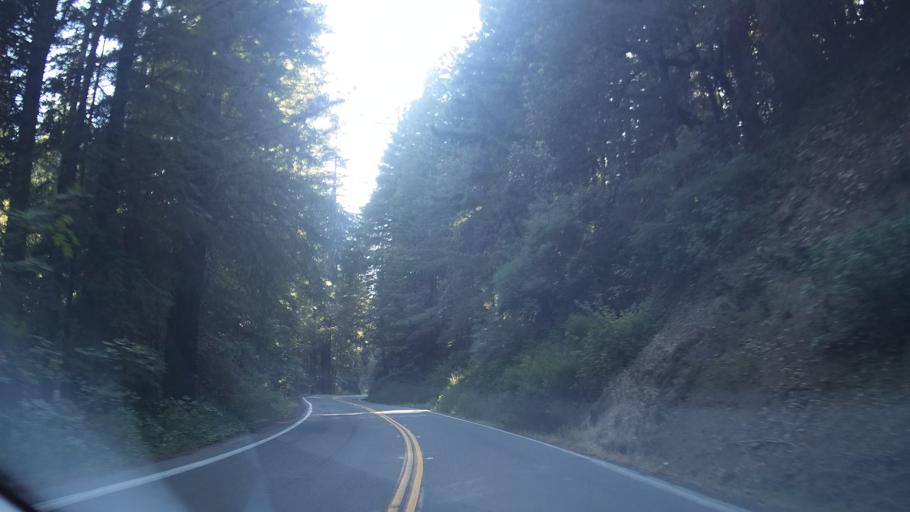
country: US
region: California
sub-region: Mendocino County
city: Brooktrails
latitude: 39.3486
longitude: -123.5163
